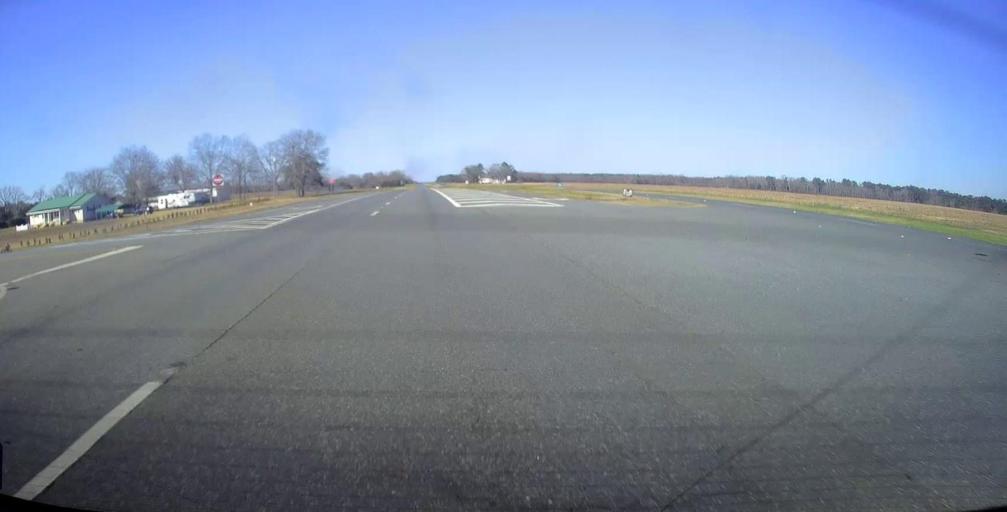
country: US
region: Georgia
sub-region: Schley County
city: Ellaville
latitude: 32.1661
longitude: -84.2696
